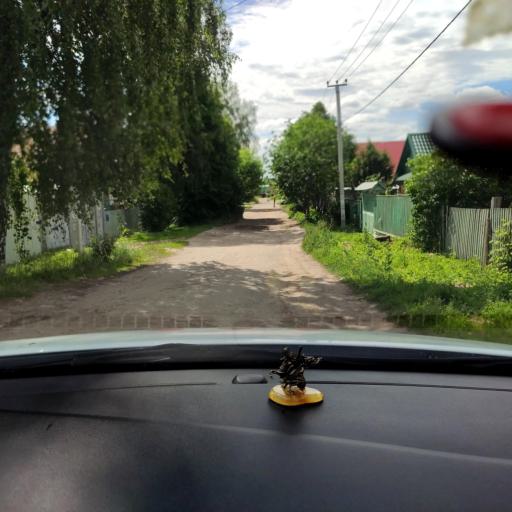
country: RU
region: Tatarstan
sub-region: Zelenodol'skiy Rayon
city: Vasil'yevo
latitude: 55.8376
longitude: 48.7213
